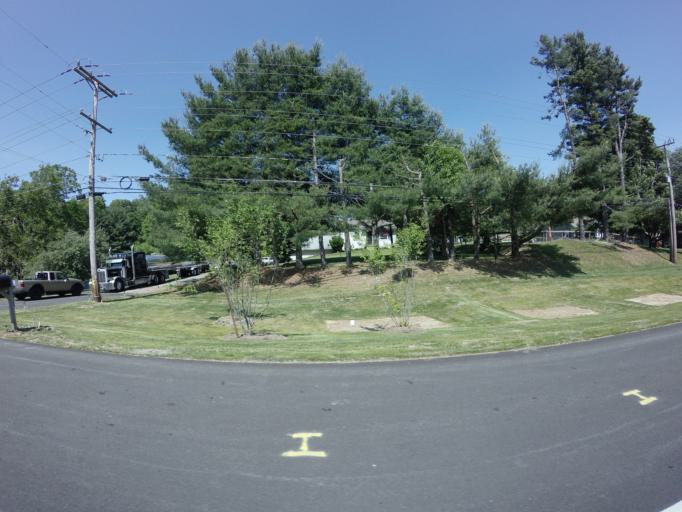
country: US
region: Maryland
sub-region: Carroll County
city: Sykesville
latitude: 39.3514
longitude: -76.9656
